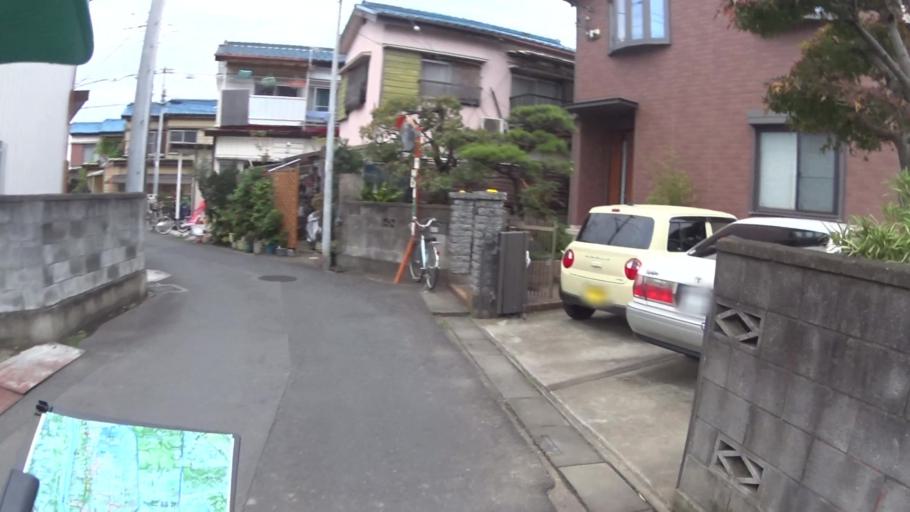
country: JP
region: Saitama
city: Yashio-shi
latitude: 35.8416
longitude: 139.8475
